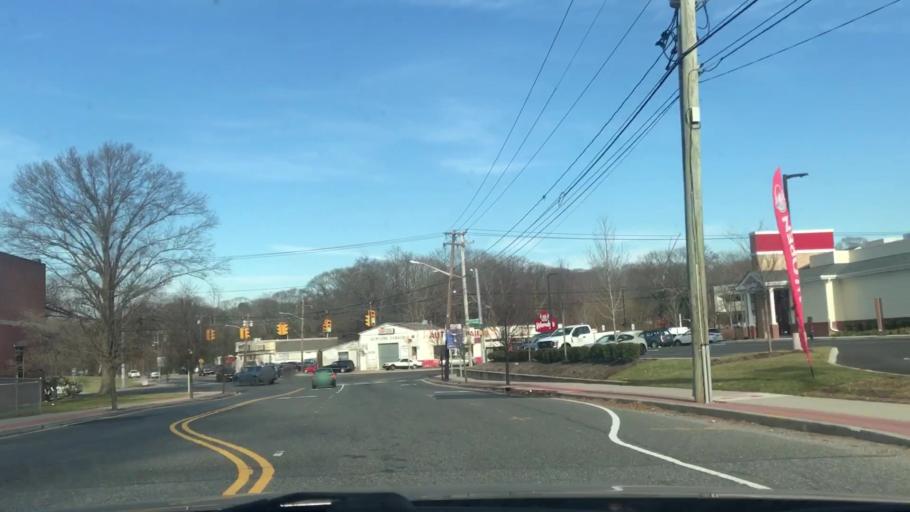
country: US
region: New York
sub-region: Suffolk County
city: Ronkonkoma
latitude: 40.8262
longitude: -73.1107
